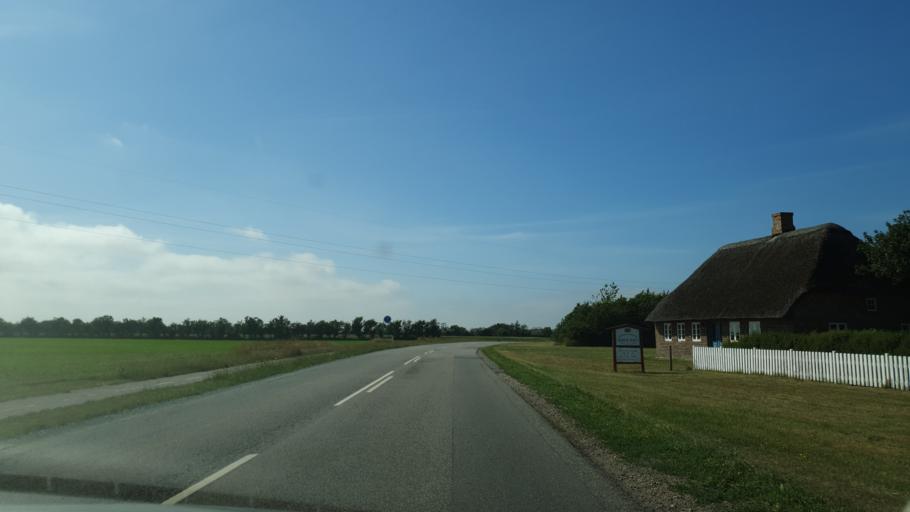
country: DK
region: Central Jutland
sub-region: Ringkobing-Skjern Kommune
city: Ringkobing
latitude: 56.0273
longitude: 8.3547
